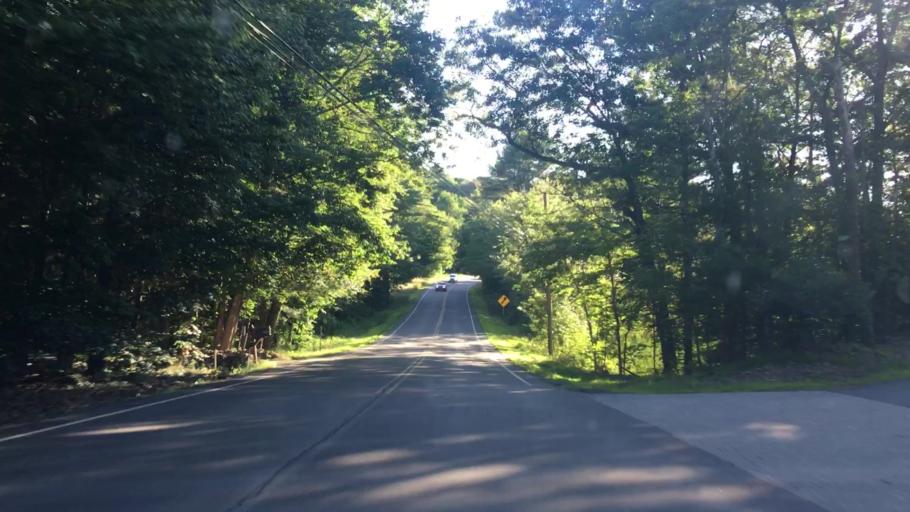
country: US
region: New Hampshire
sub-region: Rockingham County
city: Chester
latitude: 42.9542
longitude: -71.2275
